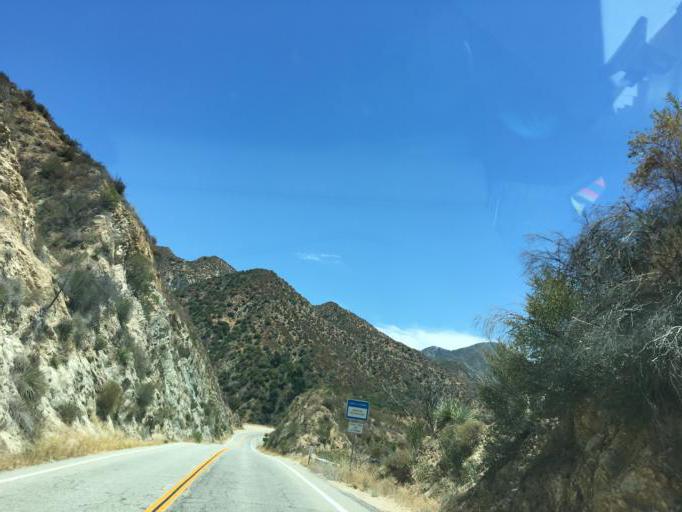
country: US
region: California
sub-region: Los Angeles County
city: La Crescenta-Montrose
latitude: 34.2899
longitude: -118.2296
